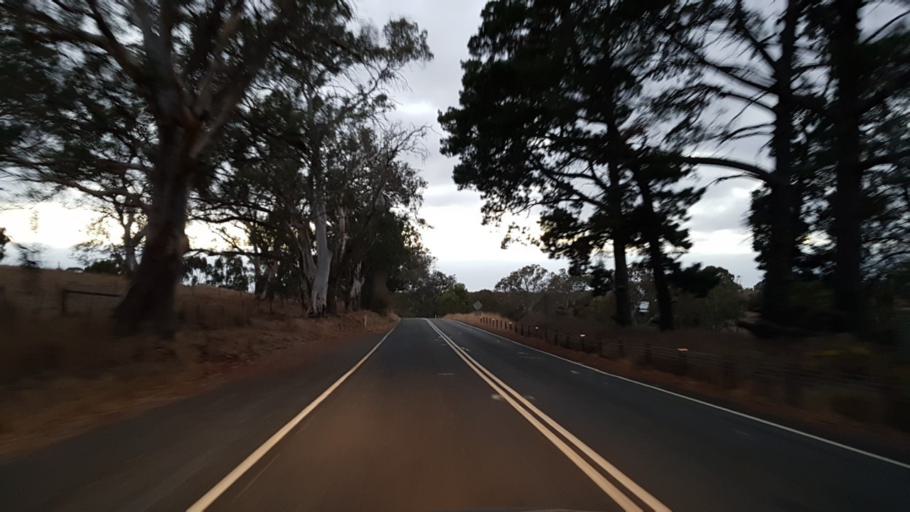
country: AU
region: South Australia
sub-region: Mount Barker
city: Nairne
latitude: -35.0312
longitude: 138.9554
